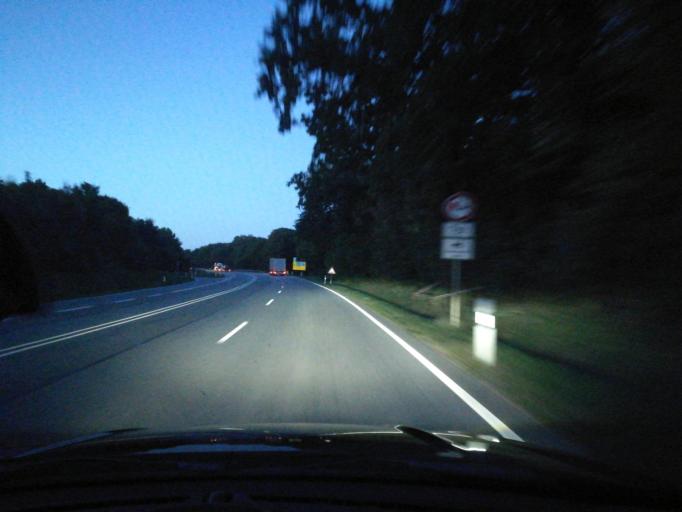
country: DE
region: Bavaria
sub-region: Lower Bavaria
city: Bad Abbach
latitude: 48.9419
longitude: 12.0444
